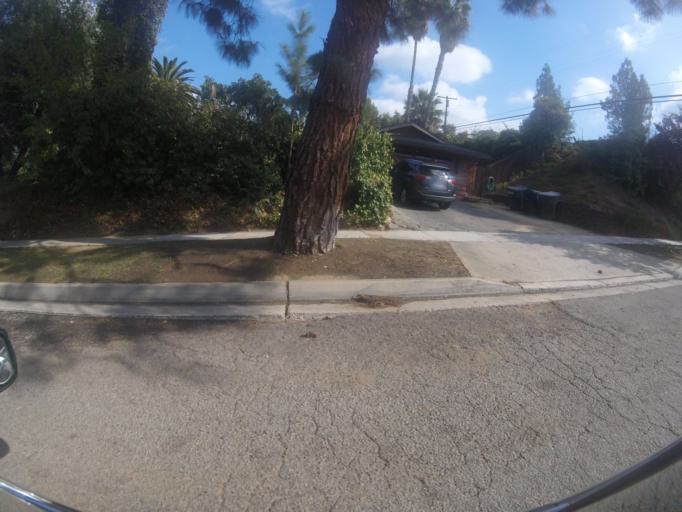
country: US
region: California
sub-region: San Bernardino County
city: Redlands
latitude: 34.0337
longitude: -117.1798
